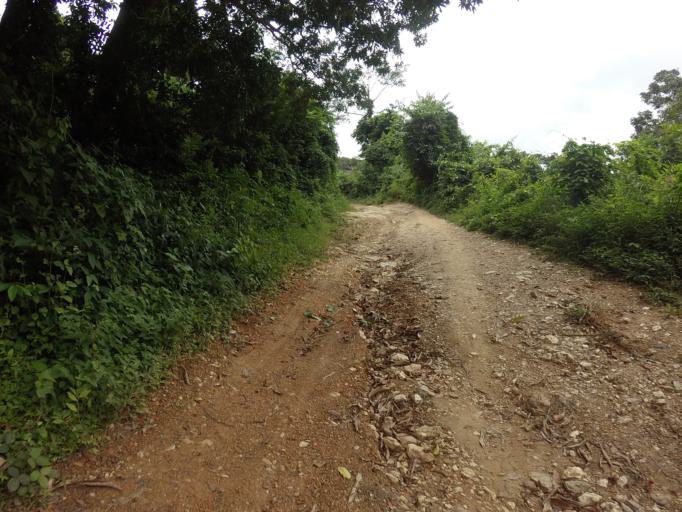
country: TG
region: Plateaux
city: Kpalime
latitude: 6.8569
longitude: 0.4418
